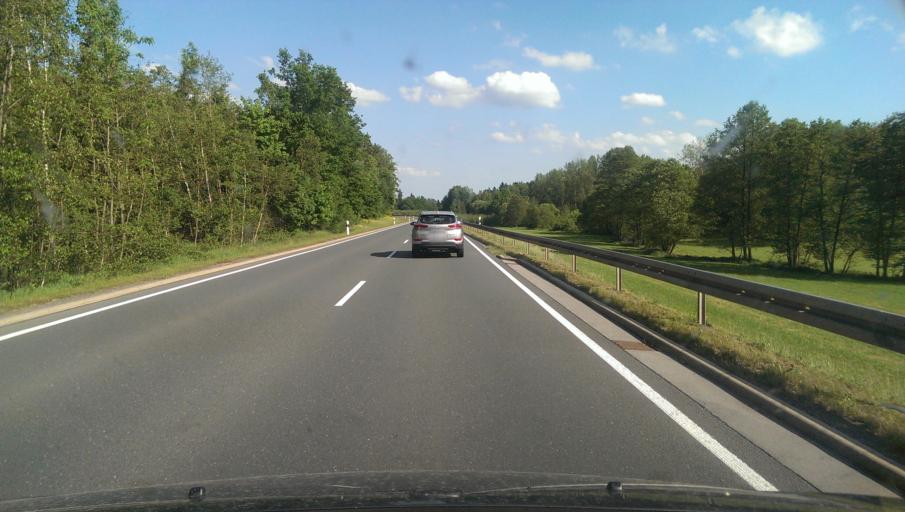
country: DE
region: Thuringia
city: Lederhose
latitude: 50.7967
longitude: 11.9329
